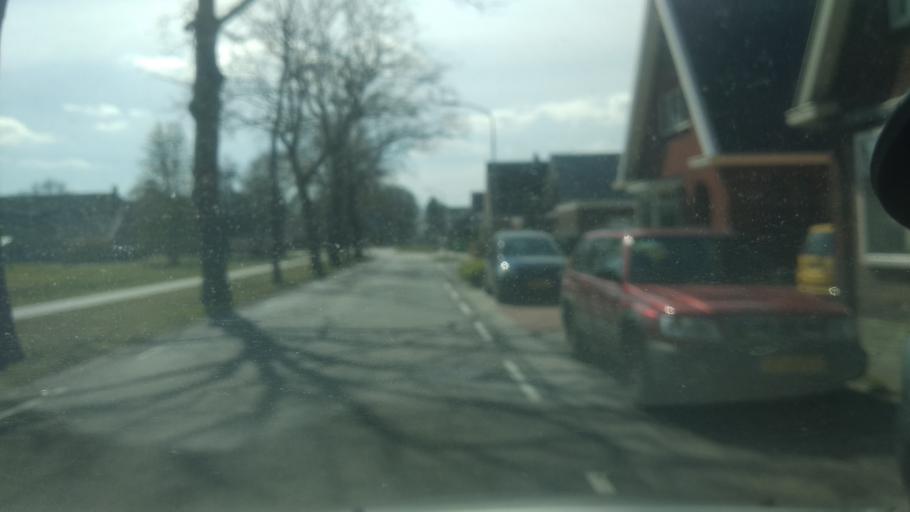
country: NL
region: Groningen
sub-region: Gemeente Stadskanaal
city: Stadskanaal
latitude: 52.9485
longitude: 6.9151
